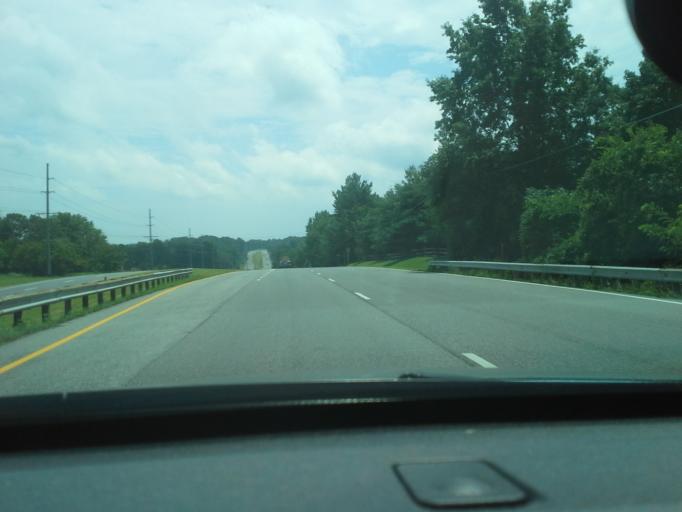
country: US
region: Maryland
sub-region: Calvert County
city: Owings
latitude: 38.6727
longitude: -76.6216
